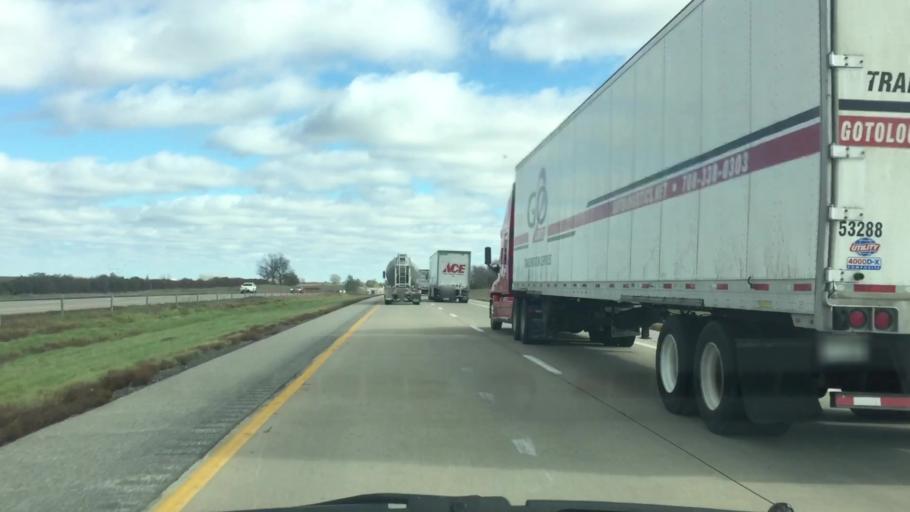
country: US
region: Iowa
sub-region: Poweshiek County
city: Brooklyn
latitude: 41.6961
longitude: -92.4155
